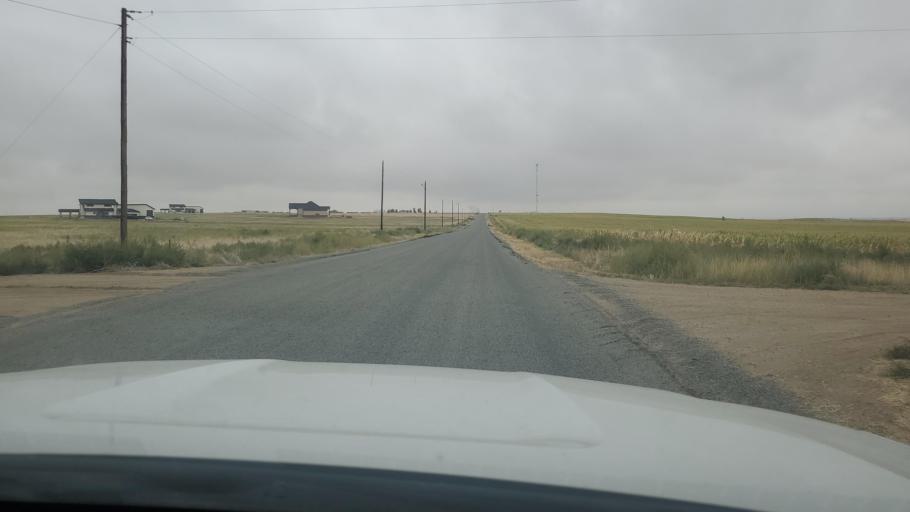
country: US
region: Colorado
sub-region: Weld County
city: Lochbuie
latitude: 39.9283
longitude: -104.6028
